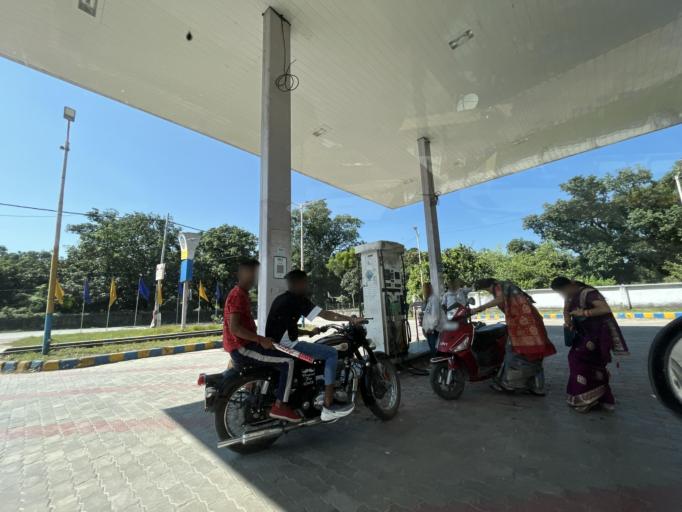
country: IN
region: Uttarakhand
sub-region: Naini Tal
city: Kaladhungi
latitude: 29.2883
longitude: 79.3442
